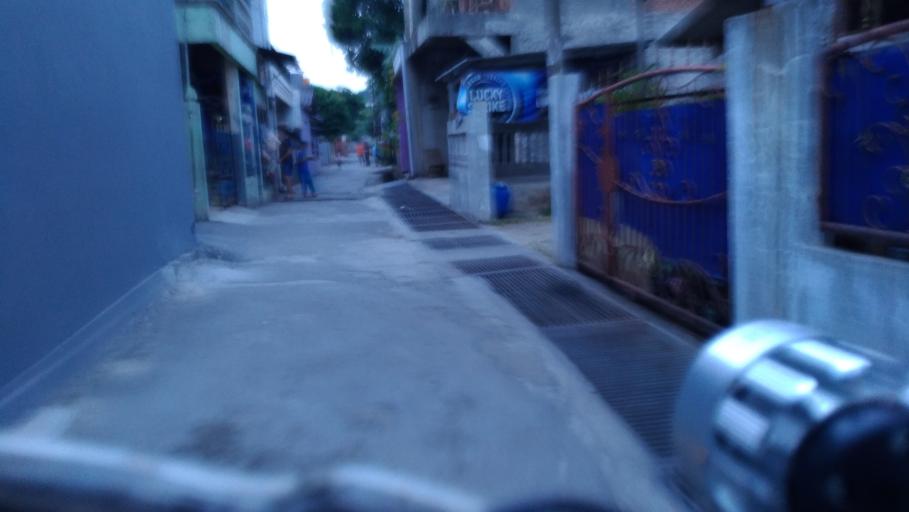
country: ID
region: West Java
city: Depok
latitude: -6.3531
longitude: 106.8762
